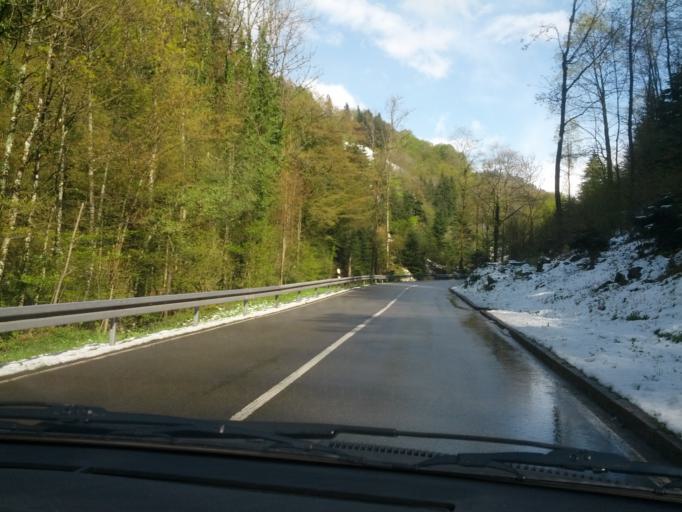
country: DE
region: Baden-Wuerttemberg
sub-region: Freiburg Region
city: Sankt Peter
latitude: 48.0288
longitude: 8.0059
